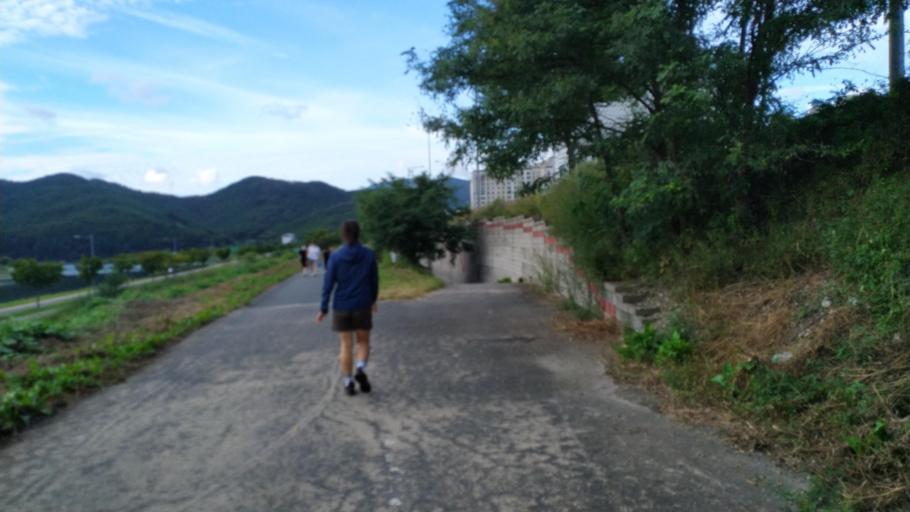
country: KR
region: Daegu
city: Daegu
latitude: 35.9204
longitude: 128.6333
